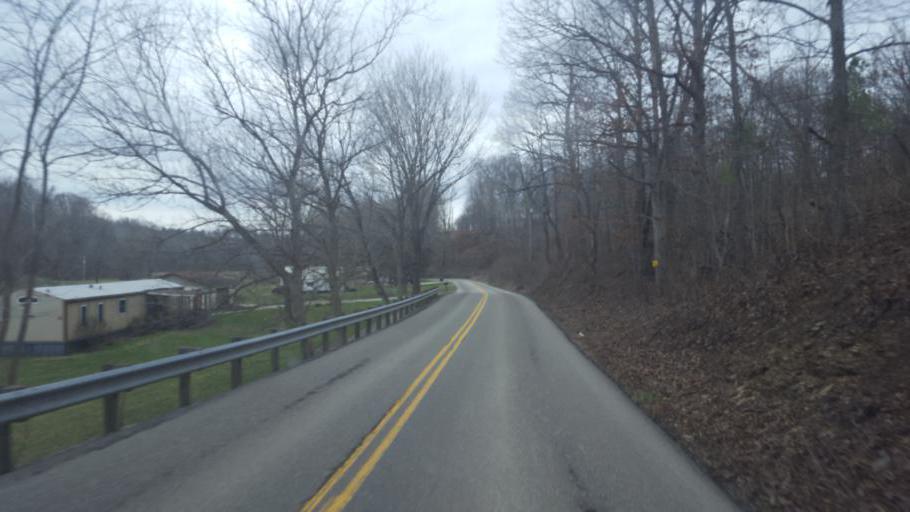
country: US
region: Ohio
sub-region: Gallia County
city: Gallipolis
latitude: 38.7230
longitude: -82.3586
